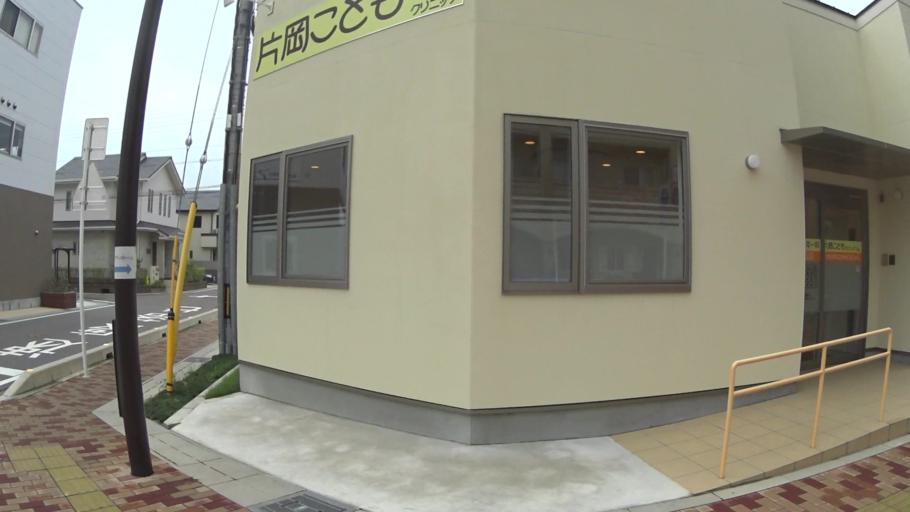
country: JP
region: Kyoto
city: Muko
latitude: 34.9632
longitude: 135.7036
